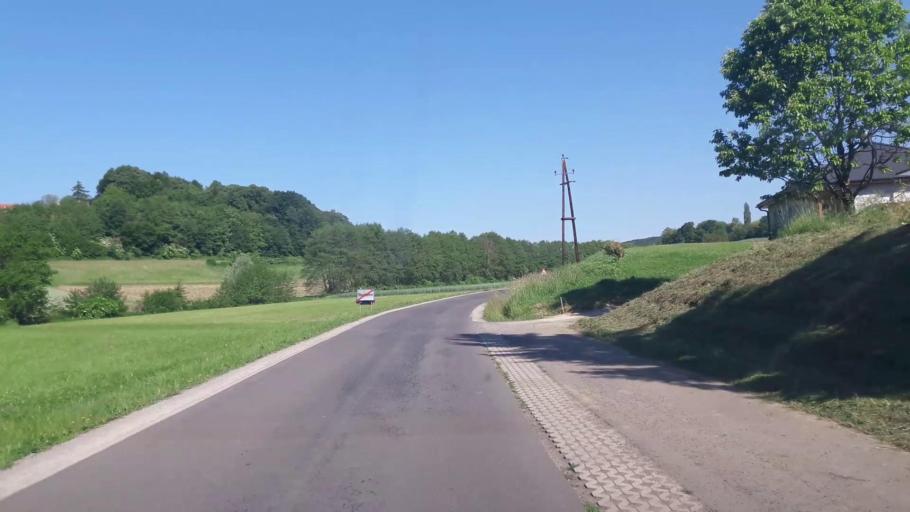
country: AT
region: Styria
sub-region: Politischer Bezirk Suedoststeiermark
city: Unterlamm
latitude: 46.9872
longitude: 16.0451
